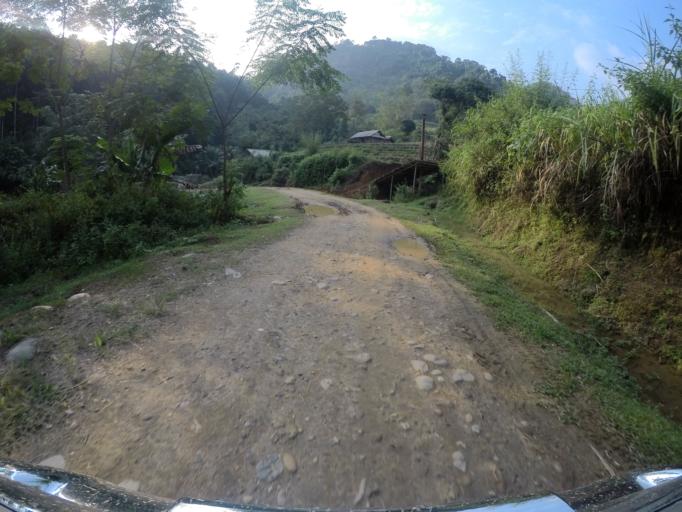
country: VN
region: Yen Bai
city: Son Thinh
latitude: 21.6877
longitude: 104.6270
